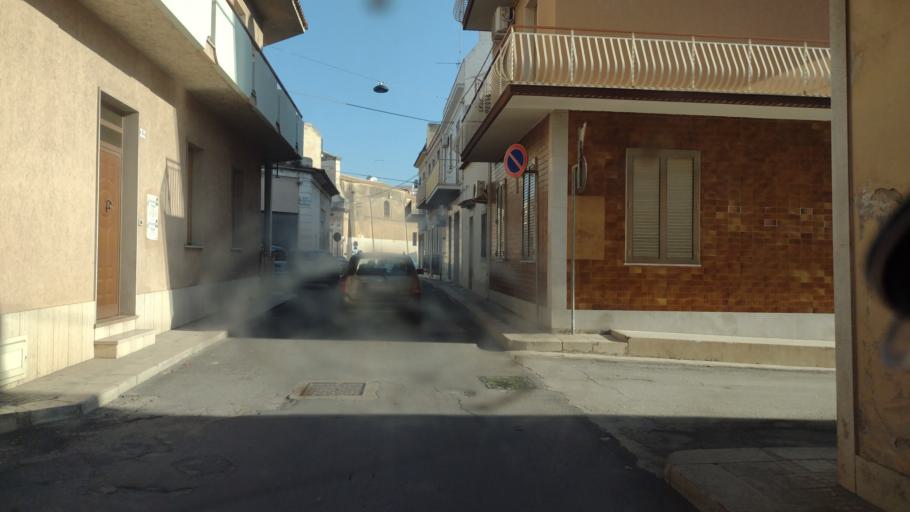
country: IT
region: Sicily
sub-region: Provincia di Siracusa
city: Avola
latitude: 36.9049
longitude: 15.1368
